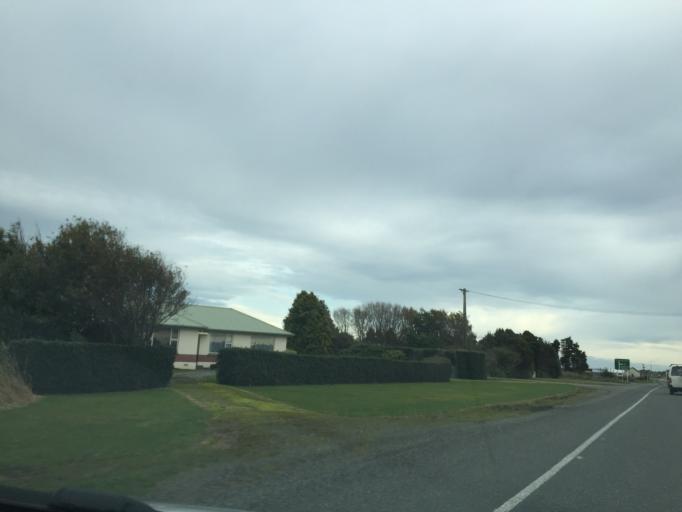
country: NZ
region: Southland
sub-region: Invercargill City
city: Invercargill
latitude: -46.3156
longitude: 168.6069
